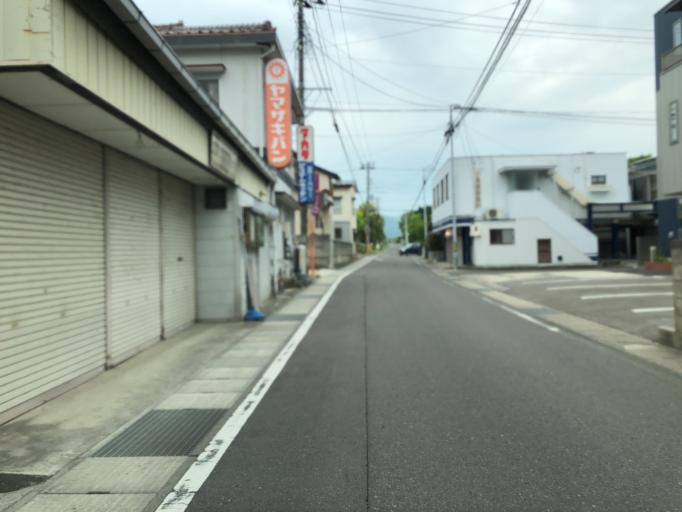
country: JP
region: Fukushima
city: Fukushima-shi
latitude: 37.7833
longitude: 140.4254
